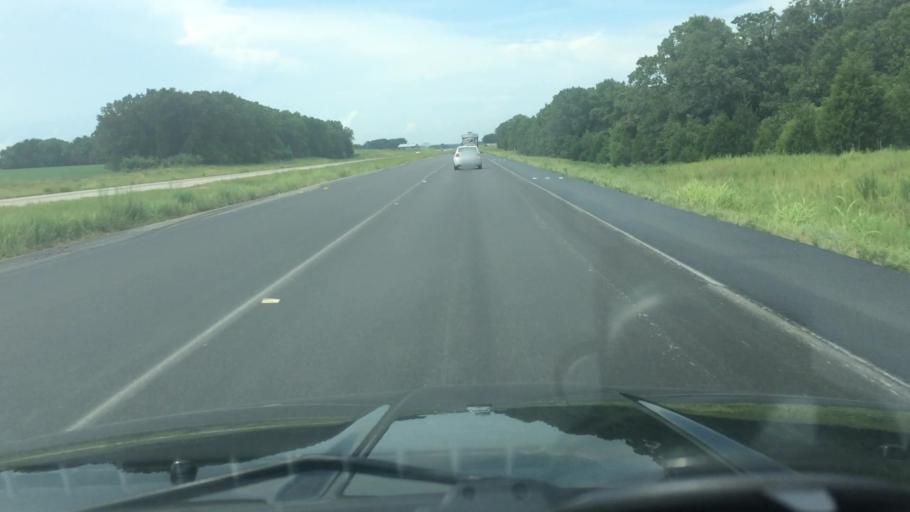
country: US
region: Missouri
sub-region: Saint Clair County
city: Osceola
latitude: 37.9679
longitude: -93.6455
